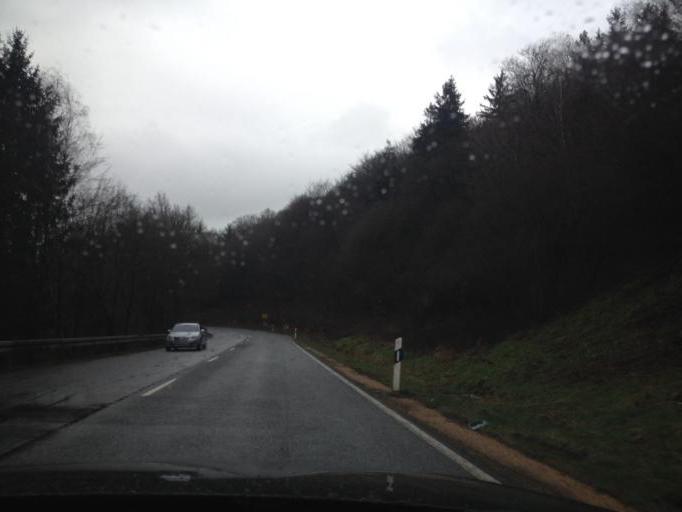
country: DE
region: Saarland
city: Nohfelden
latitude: 49.5837
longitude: 7.1517
